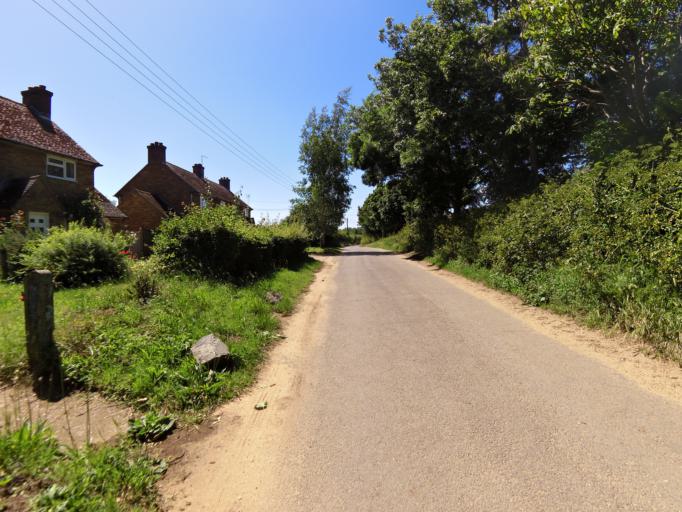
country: GB
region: England
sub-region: Suffolk
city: Felixstowe
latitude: 52.0471
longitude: 1.4376
